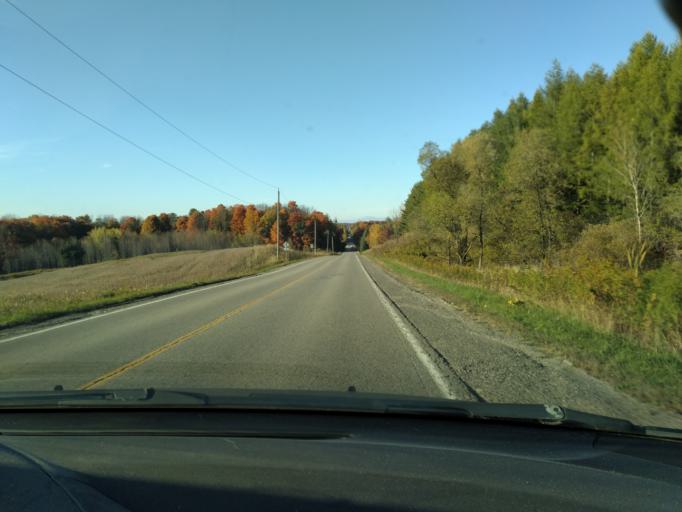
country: CA
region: Ontario
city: Bradford West Gwillimbury
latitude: 43.9656
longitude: -79.7190
